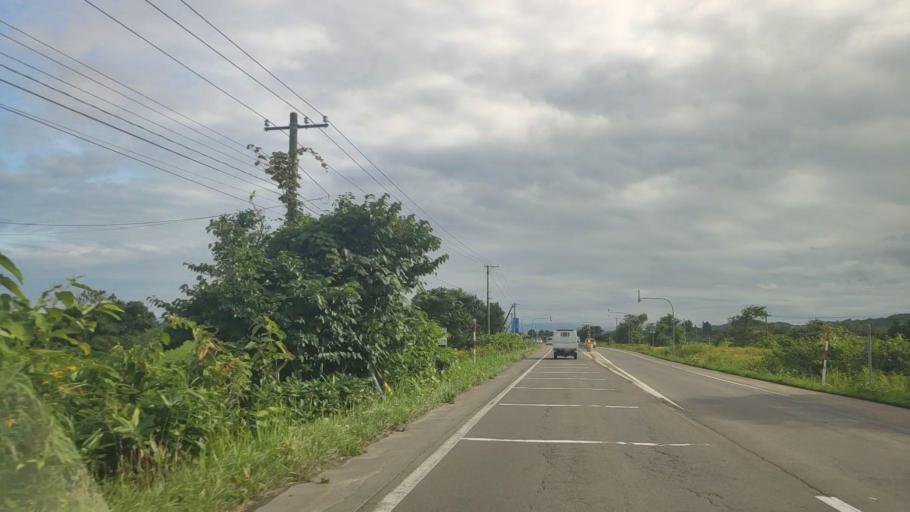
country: JP
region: Hokkaido
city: Niseko Town
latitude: 42.4566
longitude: 140.3337
